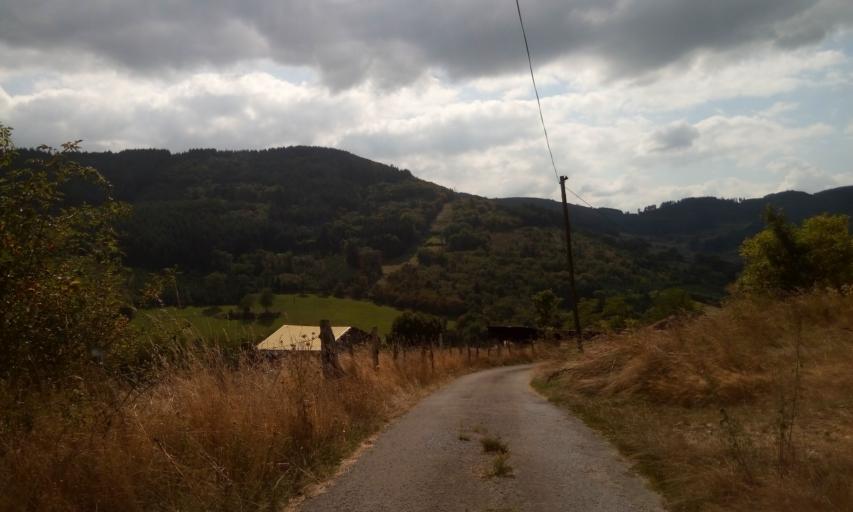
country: FR
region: Rhone-Alpes
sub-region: Departement du Rhone
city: Grandris
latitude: 46.0082
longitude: 4.4687
